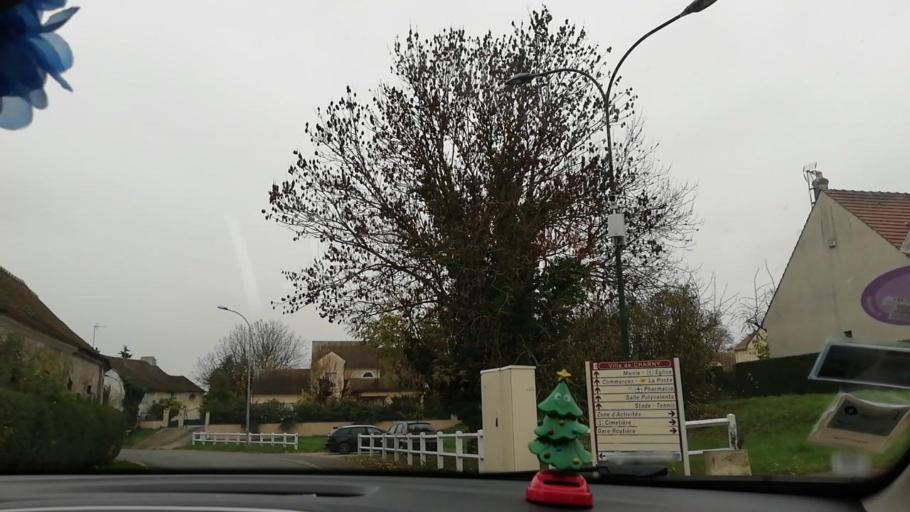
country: FR
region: Ile-de-France
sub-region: Departement de Seine-et-Marne
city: Charny
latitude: 48.9730
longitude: 2.7635
